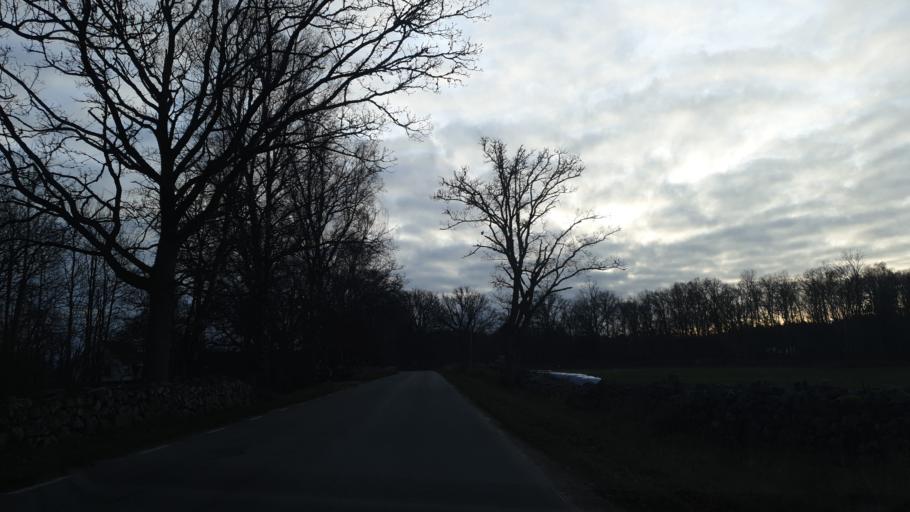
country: SE
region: Blekinge
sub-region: Karlskrona Kommun
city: Jaemjoe
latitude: 56.1778
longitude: 15.9358
